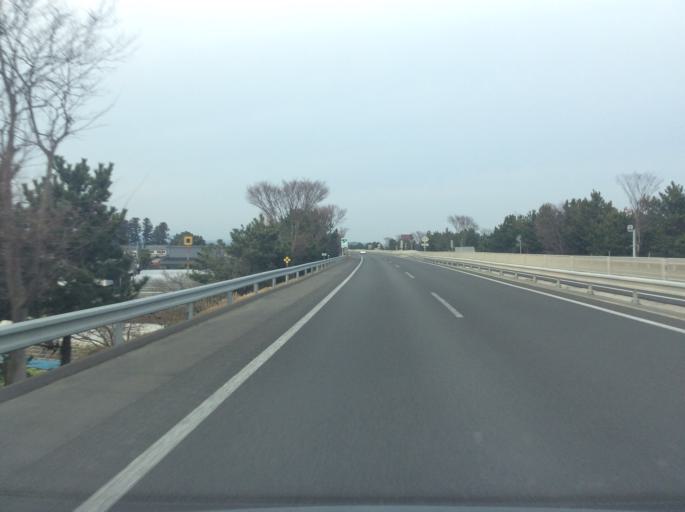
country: JP
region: Miyagi
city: Iwanuma
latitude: 38.1090
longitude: 140.8895
